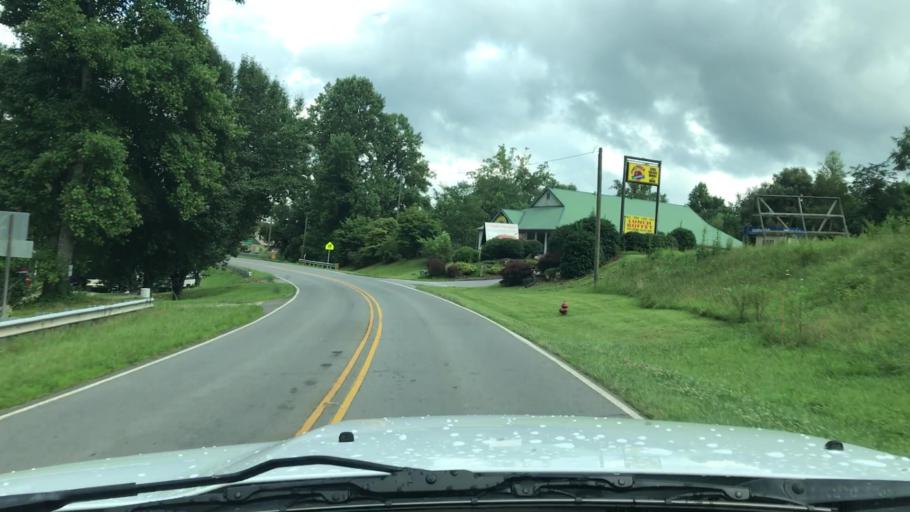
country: US
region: North Carolina
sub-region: Graham County
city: Robbinsville
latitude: 35.3296
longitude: -83.8121
